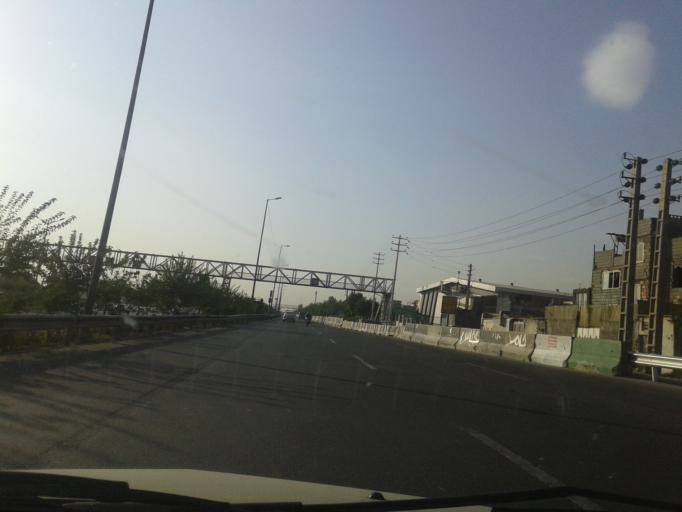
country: IR
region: Tehran
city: Eslamshahr
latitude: 35.6532
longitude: 51.2670
